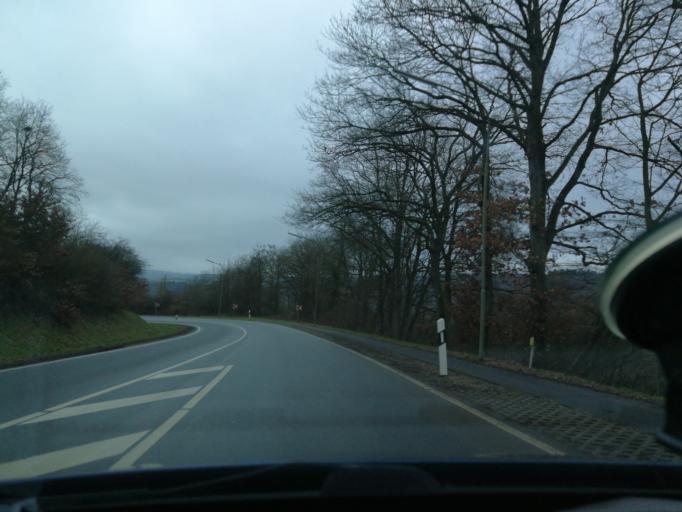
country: DE
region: Rheinland-Pfalz
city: Wittlich
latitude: 49.9994
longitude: 6.8929
